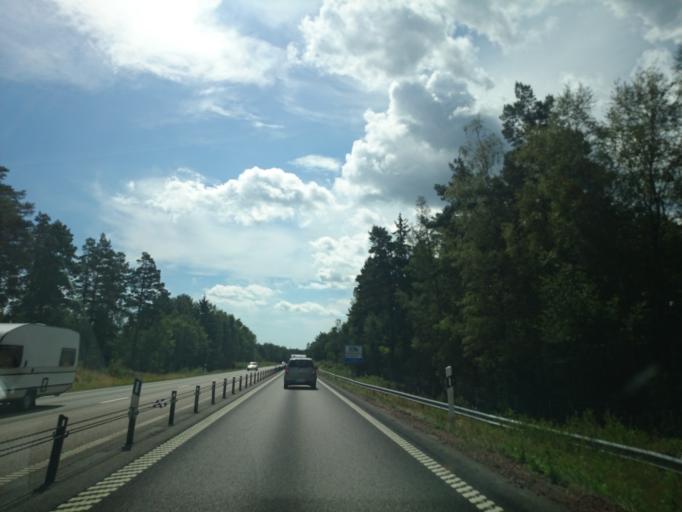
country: SE
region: Kalmar
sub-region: Oskarshamns Kommun
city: Paskallavik
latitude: 57.1878
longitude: 16.4410
